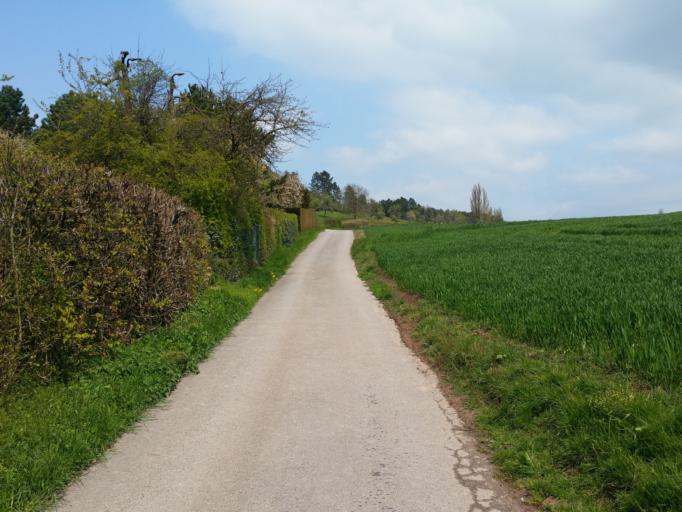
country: LU
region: Luxembourg
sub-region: Canton de Luxembourg
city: Niederanven
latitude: 49.6599
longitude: 6.2533
